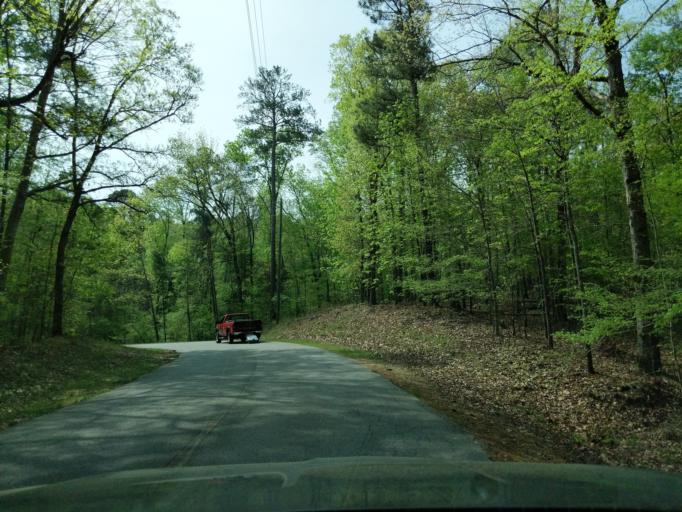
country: US
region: Georgia
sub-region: Lincoln County
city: Lincolnton
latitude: 33.8545
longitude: -82.4076
